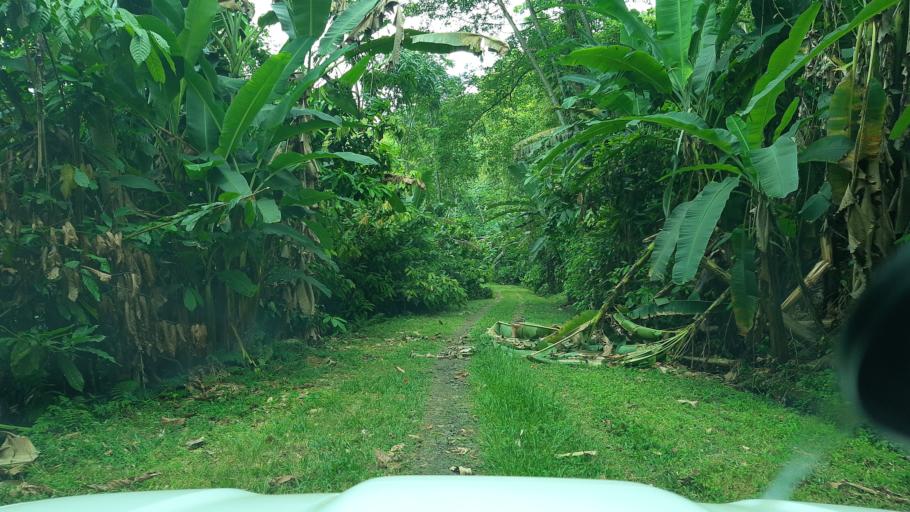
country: ST
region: Sao Tome Island
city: Sao Tome
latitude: 0.2325
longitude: 6.4733
